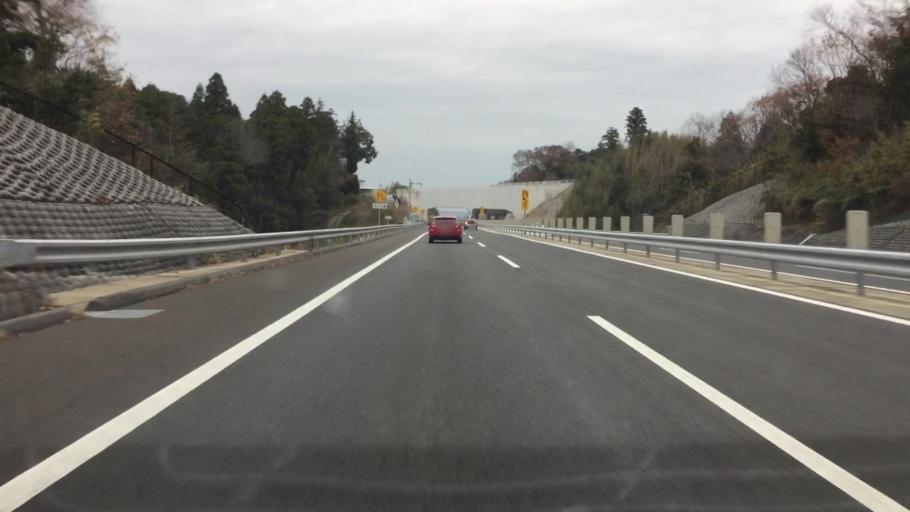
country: JP
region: Ibaraki
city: Edosaki
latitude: 35.8692
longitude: 140.3900
